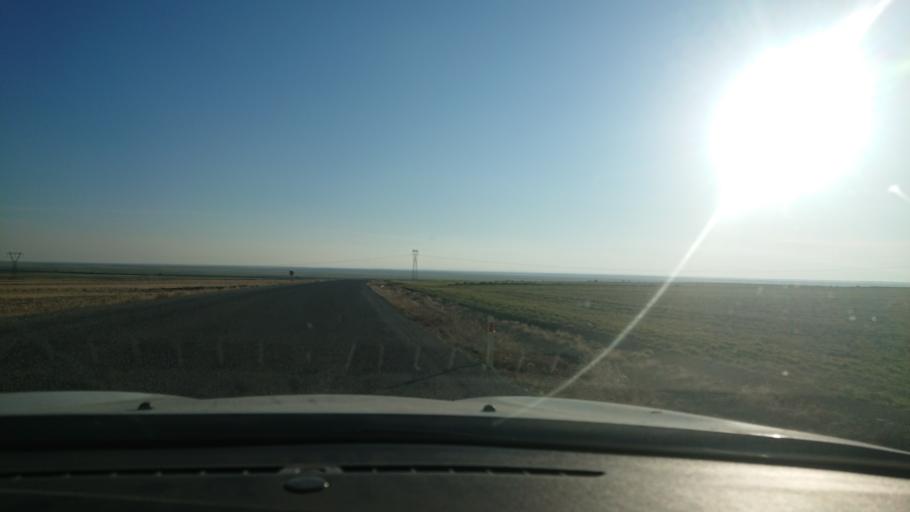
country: TR
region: Aksaray
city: Acipinar
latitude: 38.6754
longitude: 33.7304
